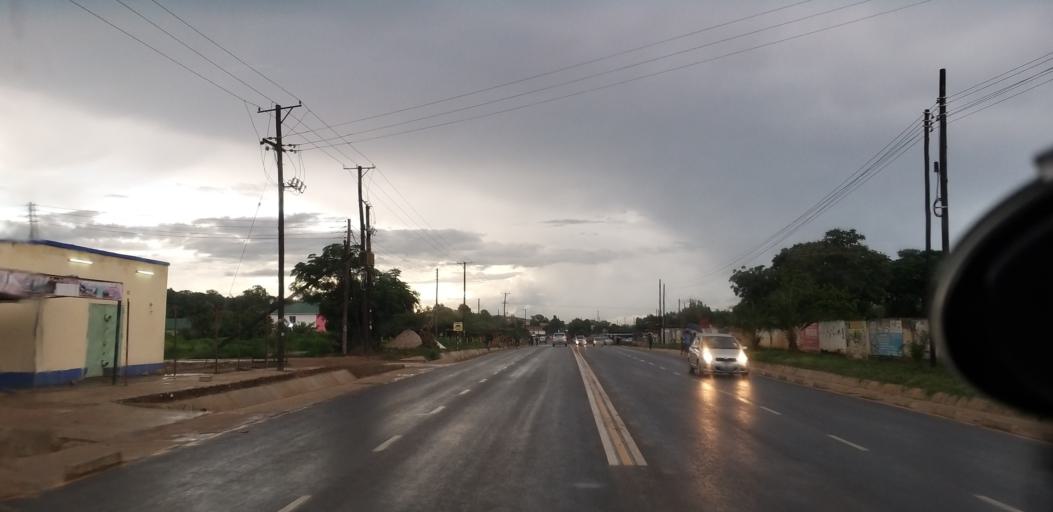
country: ZM
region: Lusaka
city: Lusaka
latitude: -15.4245
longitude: 28.3567
